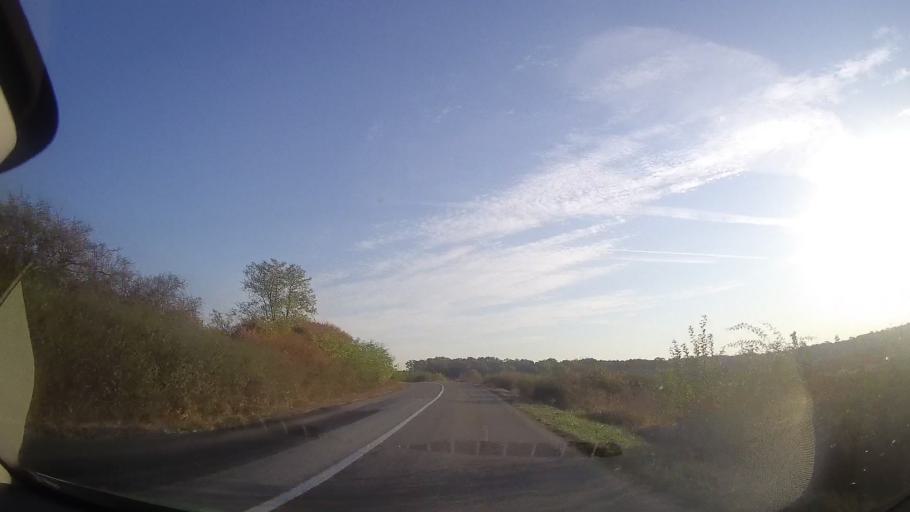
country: RO
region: Timis
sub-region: Comuna Pischia
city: Pischia
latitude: 45.9159
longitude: 21.3532
